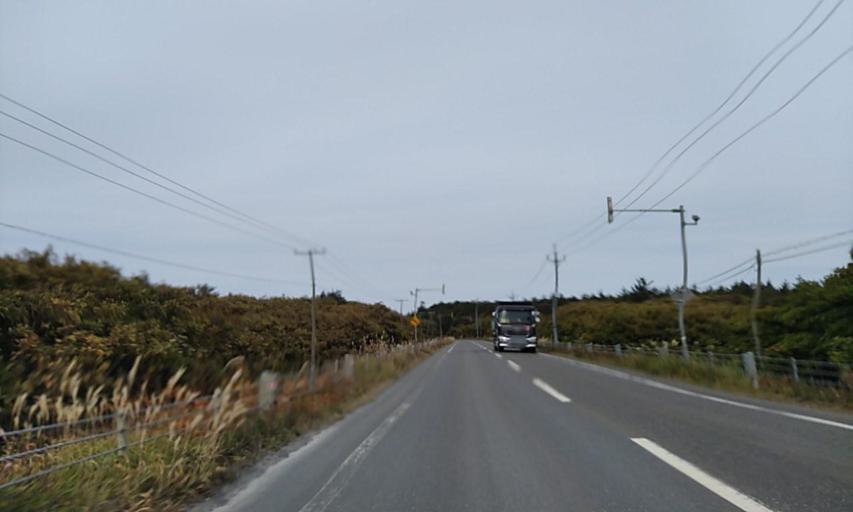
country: JP
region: Hokkaido
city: Makubetsu
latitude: 44.9969
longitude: 141.6944
